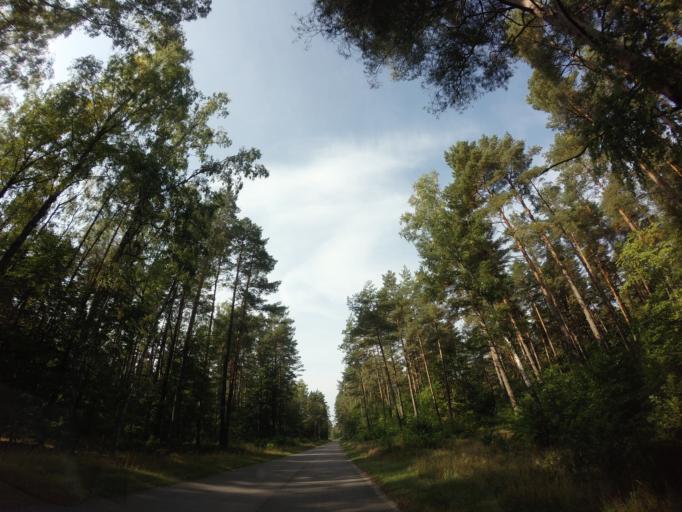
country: PL
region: West Pomeranian Voivodeship
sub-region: Powiat drawski
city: Drawsko Pomorskie
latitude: 53.4627
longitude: 15.7450
